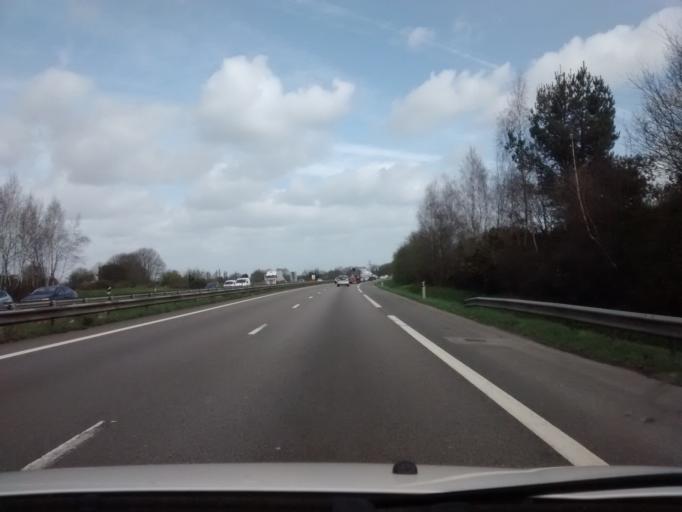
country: FR
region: Brittany
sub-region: Departement d'Ille-et-Vilaine
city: Montgermont
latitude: 48.1345
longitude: -1.7061
